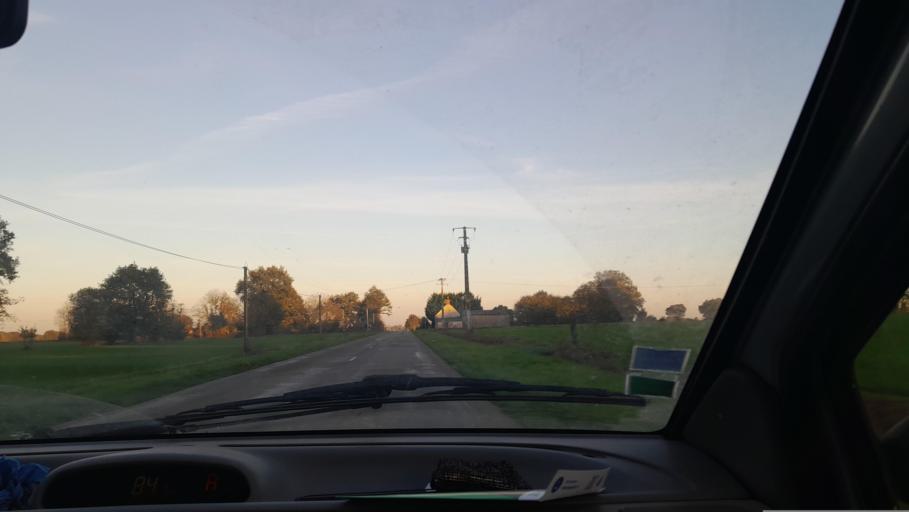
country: FR
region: Brittany
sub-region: Departement d'Ille-et-Vilaine
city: Le Pertre
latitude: 47.9689
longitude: -1.0918
